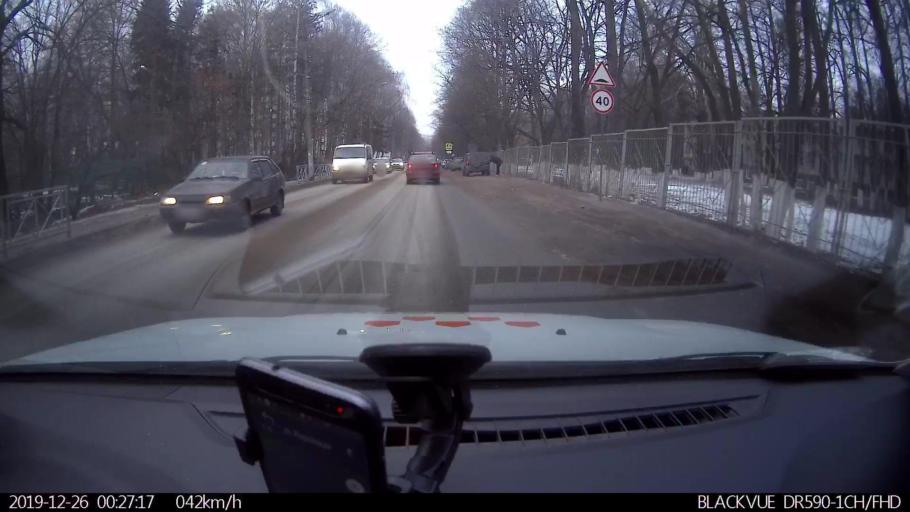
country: RU
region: Nizjnij Novgorod
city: Nizhniy Novgorod
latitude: 56.2635
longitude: 43.9993
